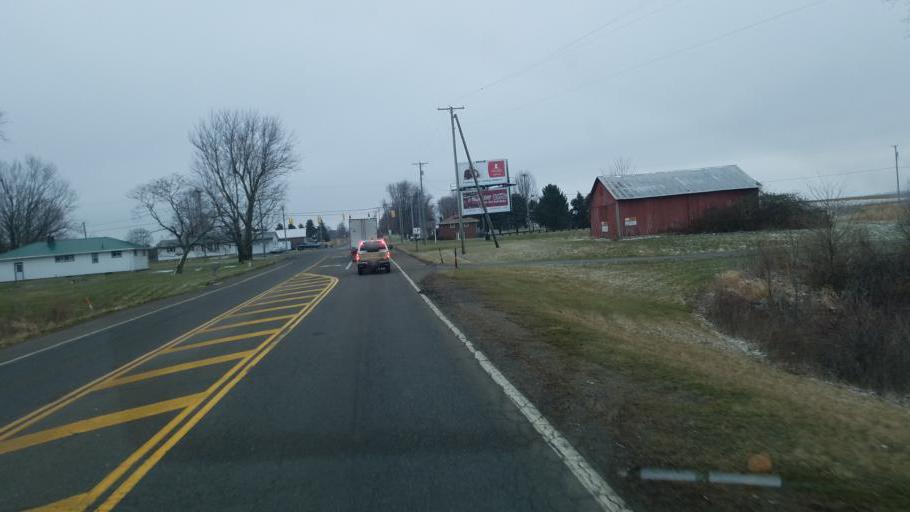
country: US
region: Ohio
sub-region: Wayne County
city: Smithville
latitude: 40.8282
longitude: -81.8423
